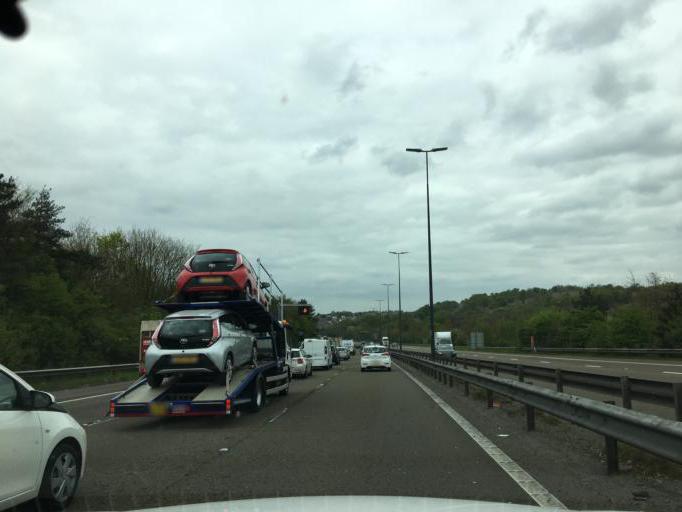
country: GB
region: Wales
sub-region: Newport
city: Newport
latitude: 51.5688
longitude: -3.0346
